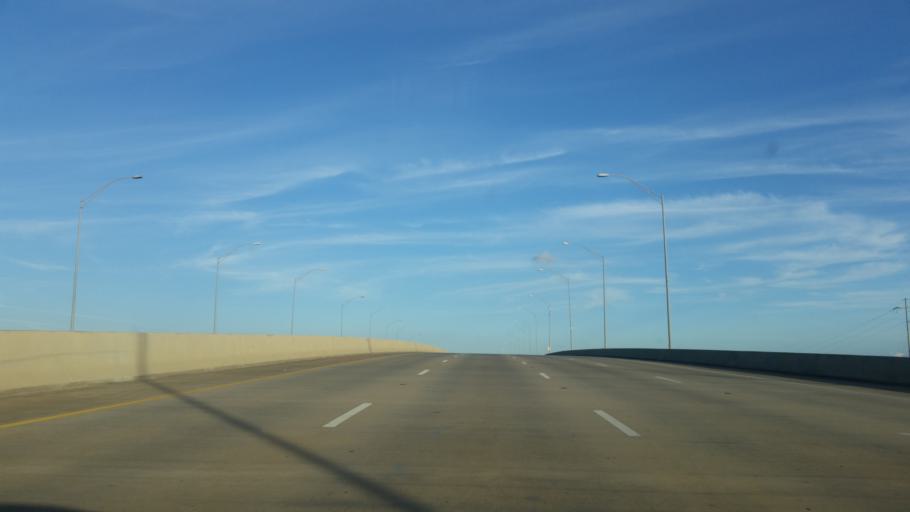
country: US
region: Mississippi
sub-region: Jackson County
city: Pascagoula
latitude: 30.3725
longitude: -88.5641
